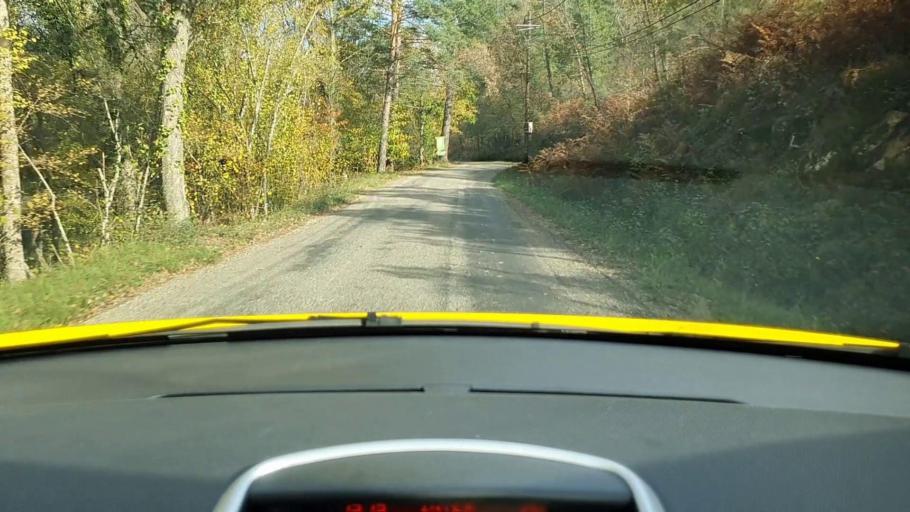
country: FR
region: Languedoc-Roussillon
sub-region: Departement du Gard
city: Lasalle
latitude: 44.0351
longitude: 3.8969
